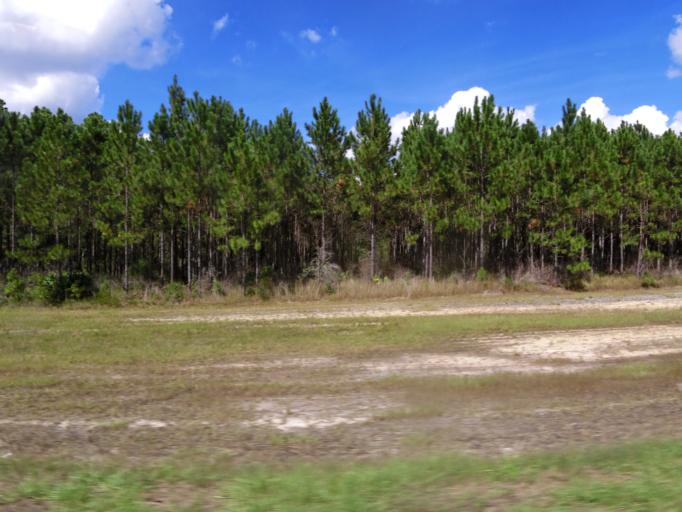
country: US
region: Florida
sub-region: Hamilton County
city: Jasper
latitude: 30.6740
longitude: -82.6696
